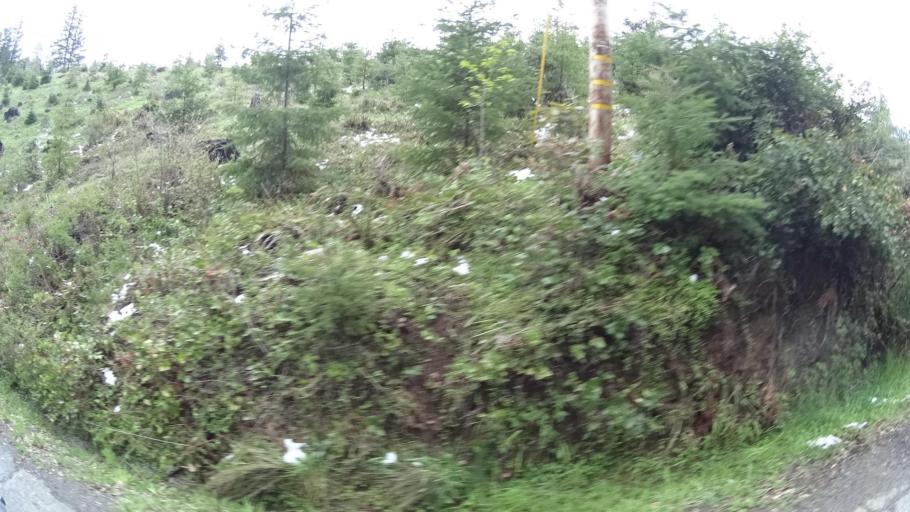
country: US
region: California
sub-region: Humboldt County
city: Blue Lake
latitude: 40.8676
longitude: -123.9035
